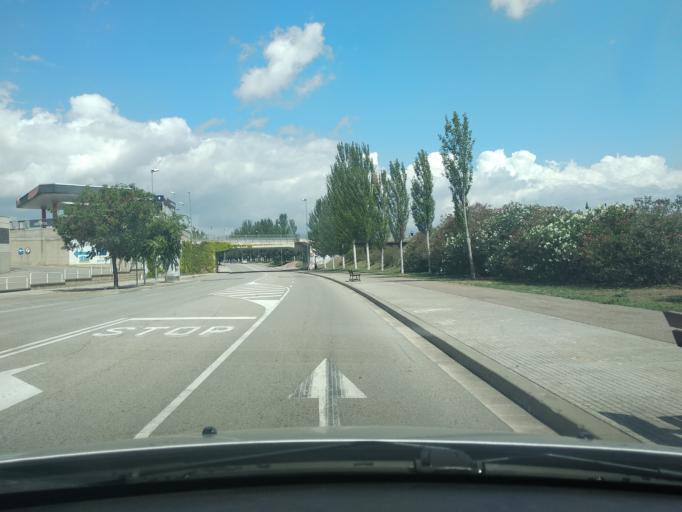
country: ES
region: Catalonia
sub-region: Provincia de Barcelona
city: Granollers
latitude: 41.6007
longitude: 2.2783
